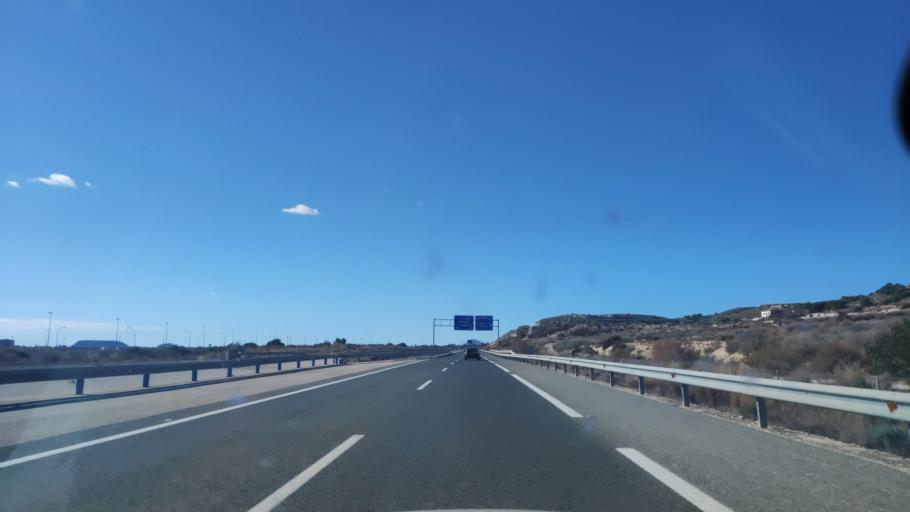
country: ES
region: Valencia
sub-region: Provincia de Alicante
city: el Campello
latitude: 38.4450
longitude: -0.3928
